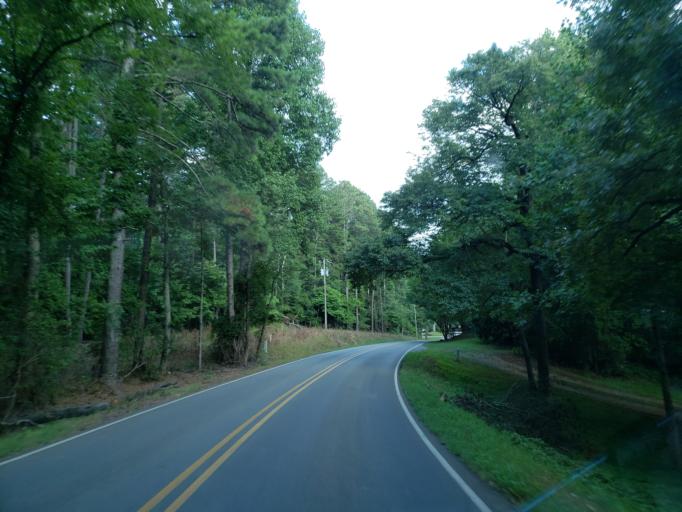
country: US
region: Georgia
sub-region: Cherokee County
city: Ball Ground
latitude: 34.3354
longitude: -84.4407
